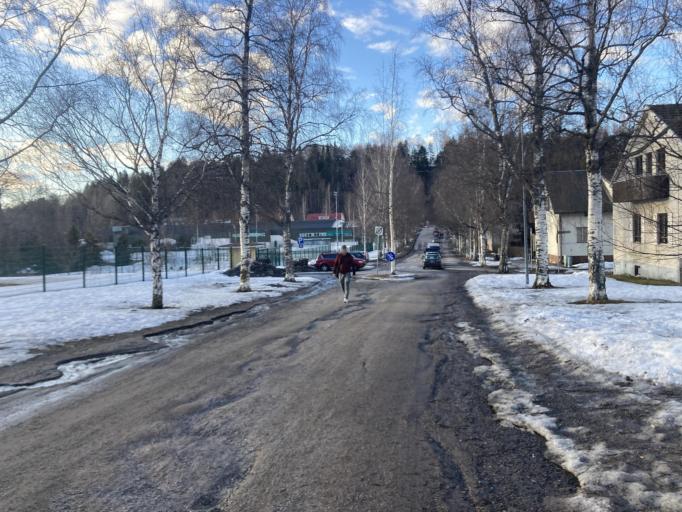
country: FI
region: Paijanne Tavastia
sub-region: Lahti
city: Lahti
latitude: 60.9875
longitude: 25.6538
